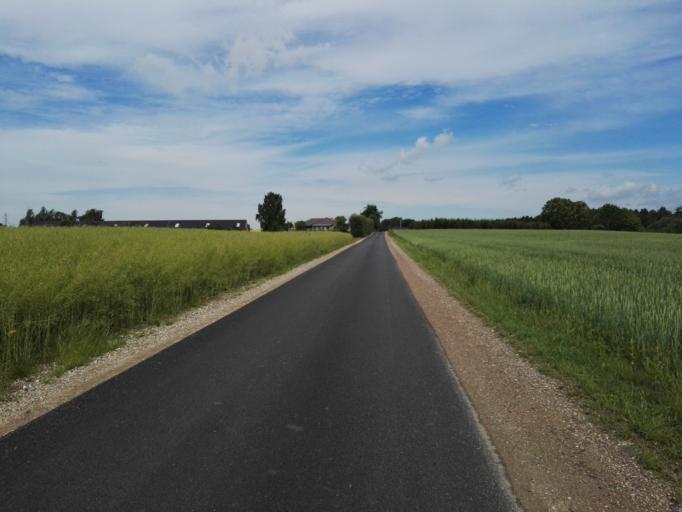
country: DK
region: Capital Region
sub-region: Egedal Kommune
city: Olstykke
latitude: 55.8123
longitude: 12.1777
